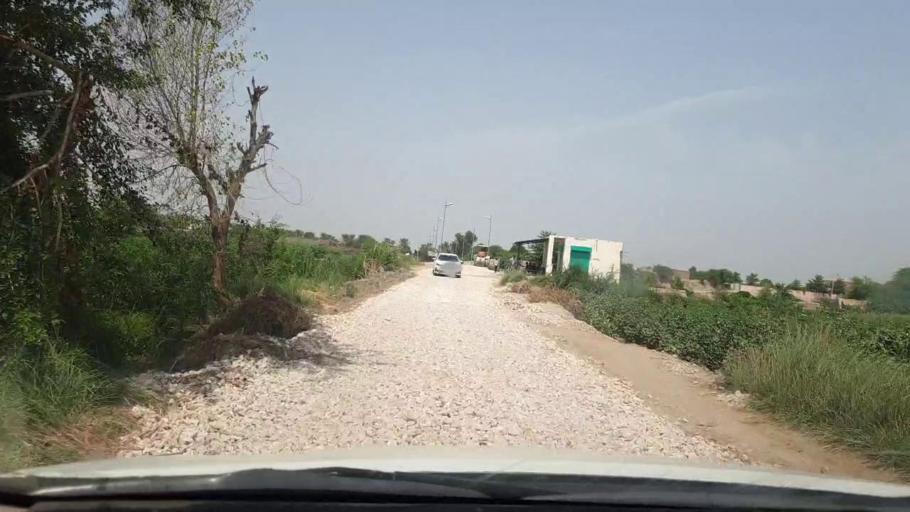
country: PK
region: Sindh
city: Rohri
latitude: 27.4957
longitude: 69.0266
